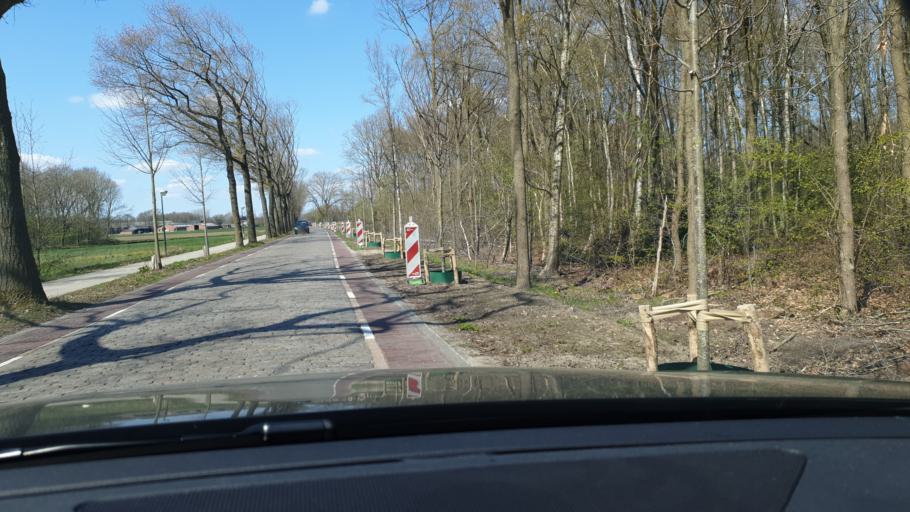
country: NL
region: North Brabant
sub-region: Gemeente Bladel en Netersel
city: Bladel
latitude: 51.3989
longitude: 5.2308
